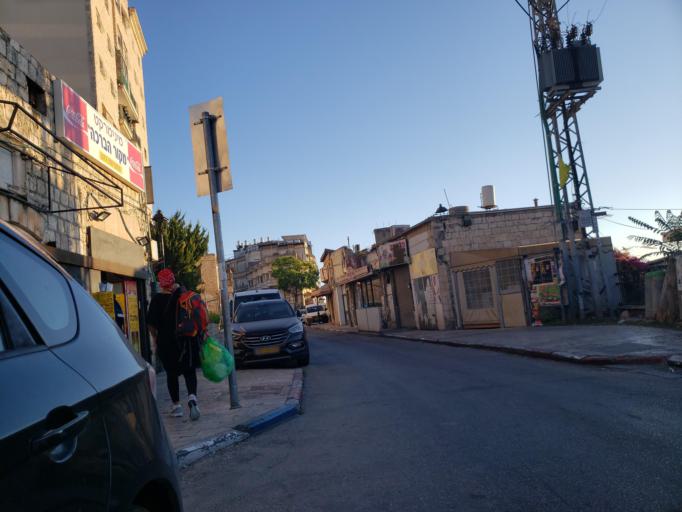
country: IL
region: Northern District
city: Safed
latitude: 32.9709
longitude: 35.4937
